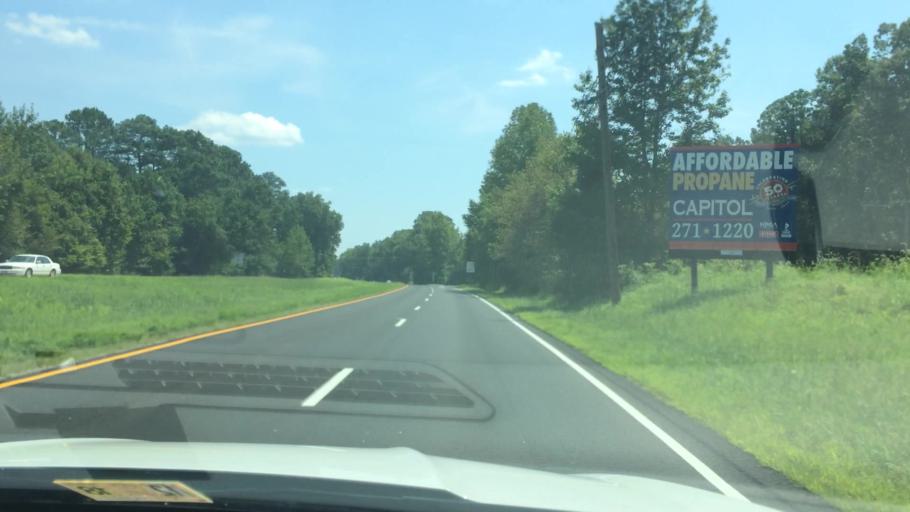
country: US
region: Virginia
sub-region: Charles City County
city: Charles City
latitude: 37.4436
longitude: -77.0524
